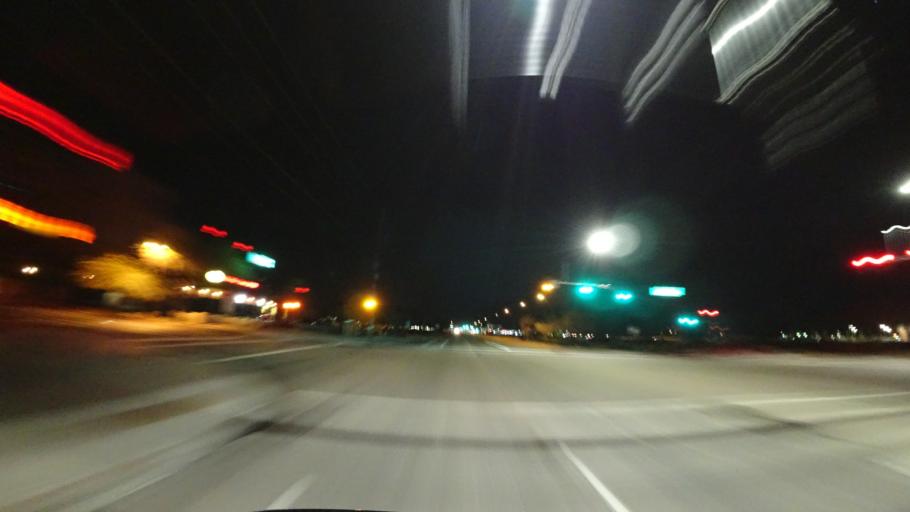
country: US
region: Arizona
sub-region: Maricopa County
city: San Carlos
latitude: 33.3498
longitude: -111.8291
